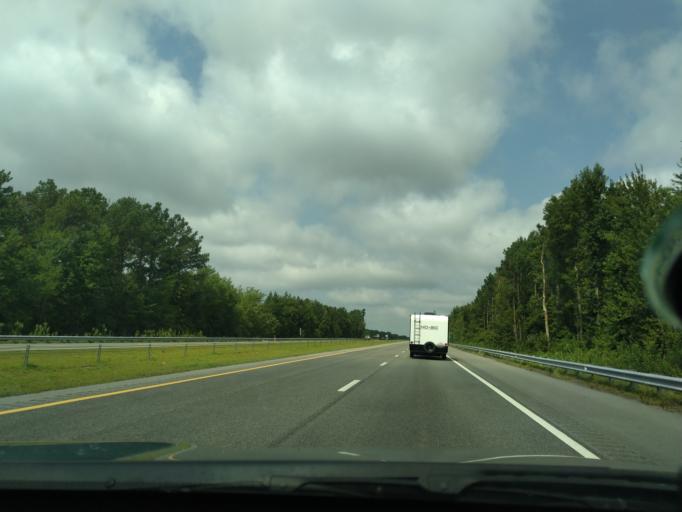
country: US
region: North Carolina
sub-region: Pitt County
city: Bethel
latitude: 35.8318
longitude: -77.3429
